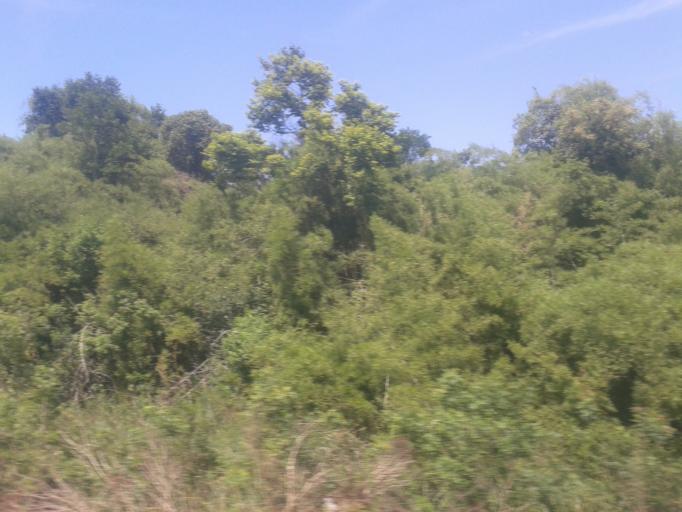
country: AR
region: Misiones
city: Bonpland
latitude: -27.4220
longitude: -55.5177
